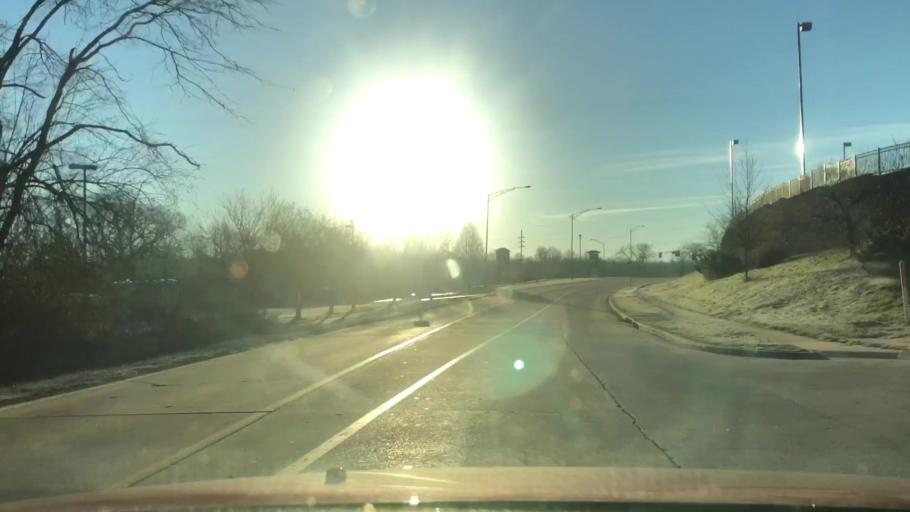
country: US
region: Missouri
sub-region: Greene County
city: Springfield
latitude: 37.1601
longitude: -93.2422
